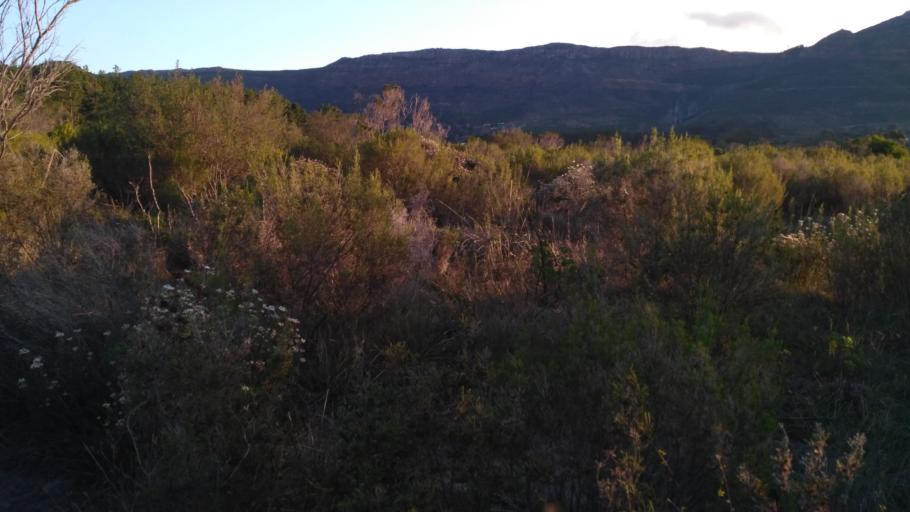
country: ZA
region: Western Cape
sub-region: City of Cape Town
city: Bergvliet
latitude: -34.0539
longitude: 18.4346
